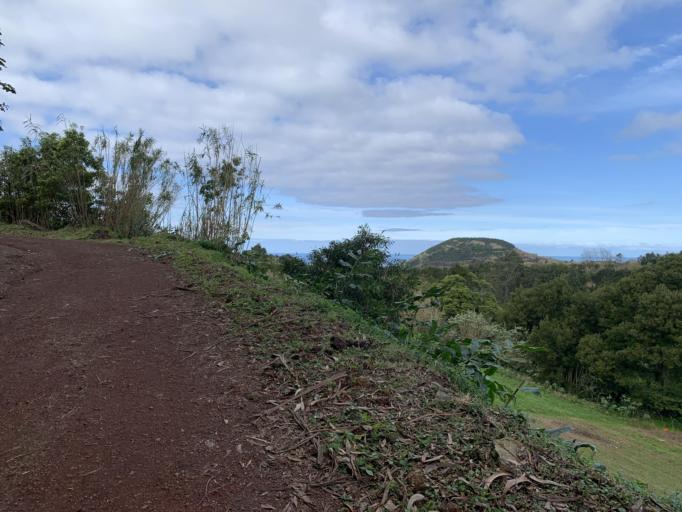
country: PT
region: Azores
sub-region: Ribeira Grande
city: Rabo de Peixe
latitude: 37.8042
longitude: -25.5028
